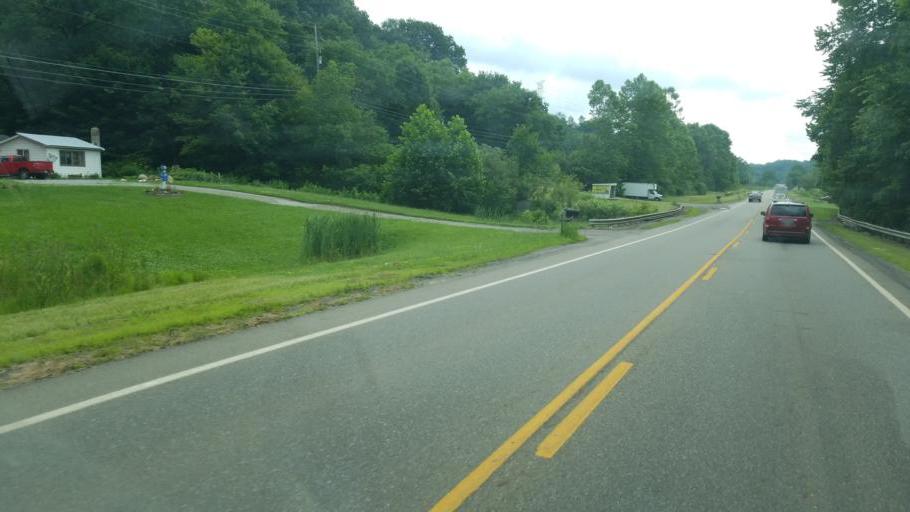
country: US
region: Ohio
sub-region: Columbiana County
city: Lisbon
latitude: 40.7700
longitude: -80.7444
